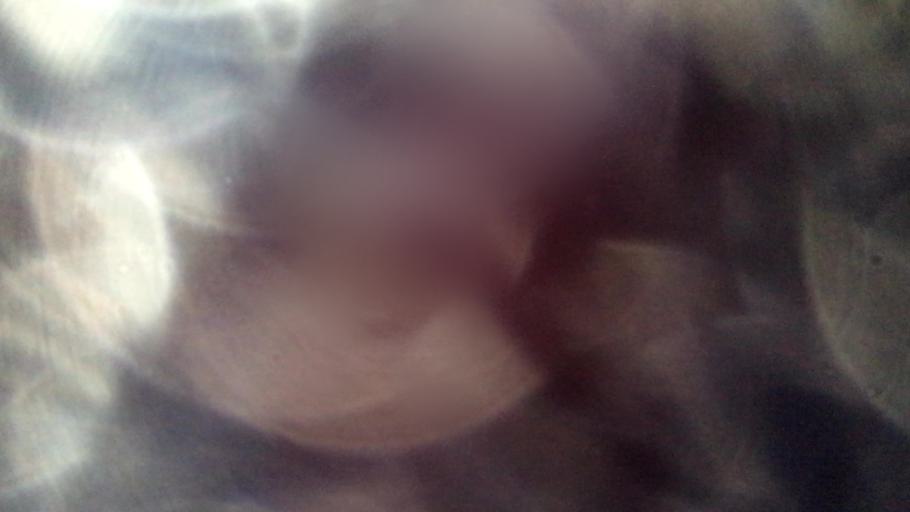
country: US
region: New Jersey
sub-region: Hudson County
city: Guttenberg
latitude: 40.7802
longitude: -74.0007
